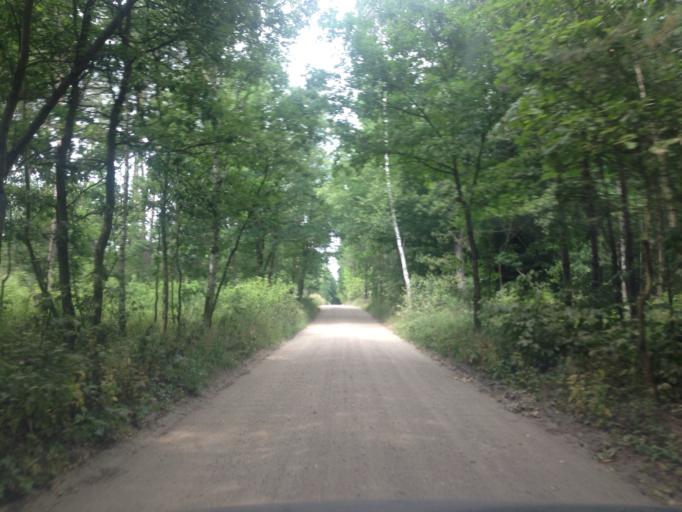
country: PL
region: Kujawsko-Pomorskie
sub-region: Powiat golubsko-dobrzynski
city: Radomin
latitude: 53.1444
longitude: 19.1413
